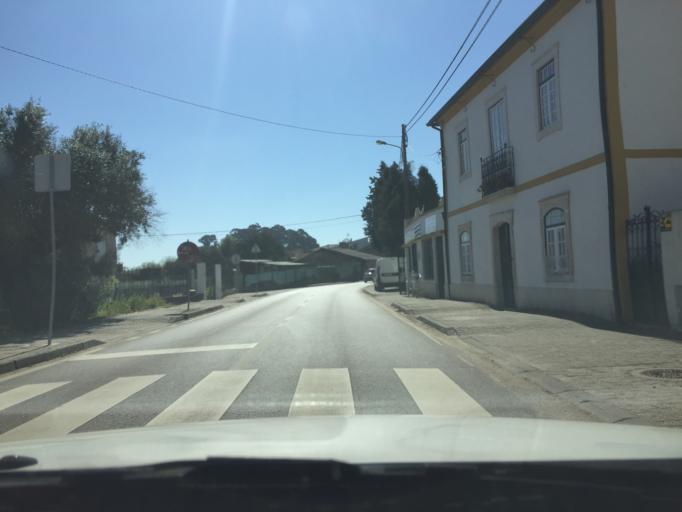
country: PT
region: Aveiro
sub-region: Anadia
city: Sangalhos
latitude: 40.4214
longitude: -8.5297
